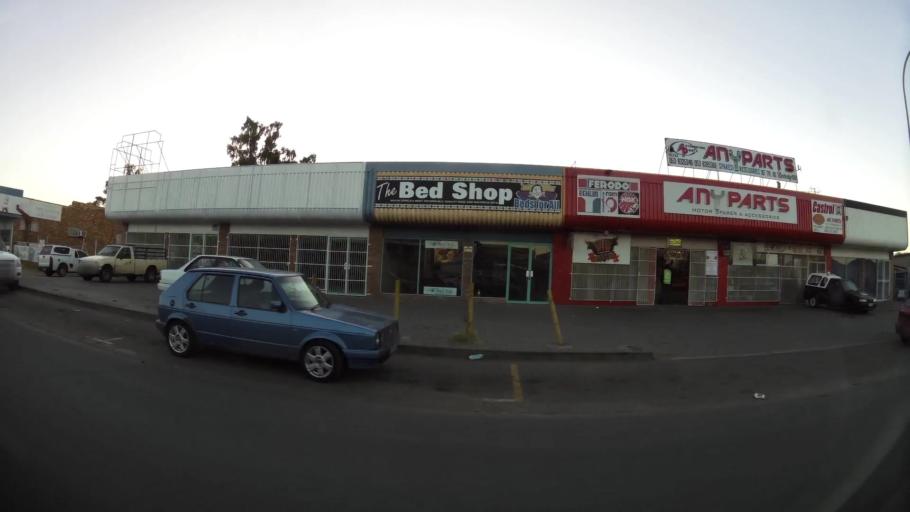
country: ZA
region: Northern Cape
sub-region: Frances Baard District Municipality
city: Kimberley
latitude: -28.7303
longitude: 24.7651
